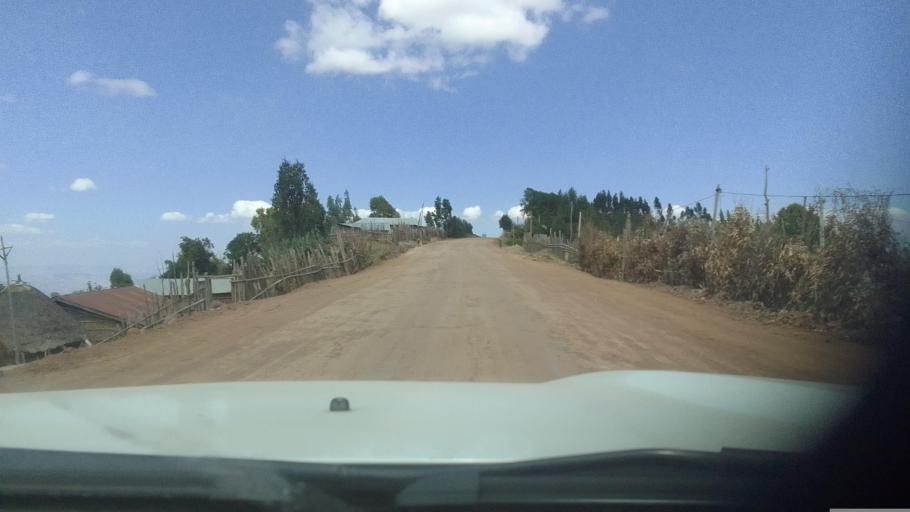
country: ET
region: Oromiya
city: Hagere Hiywet
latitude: 8.8396
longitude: 37.8857
